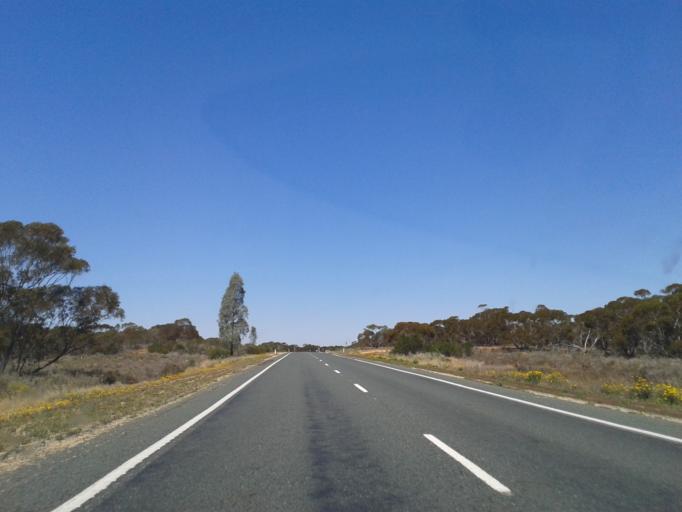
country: AU
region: New South Wales
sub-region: Wentworth
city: Gol Gol
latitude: -34.3799
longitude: 142.4209
